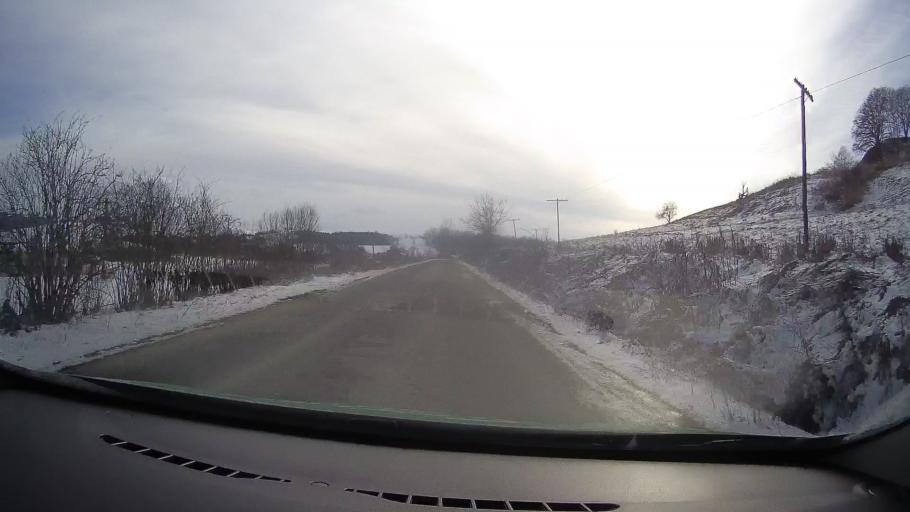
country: RO
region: Sibiu
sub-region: Comuna Iacobeni
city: Iacobeni
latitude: 46.0182
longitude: 24.6958
